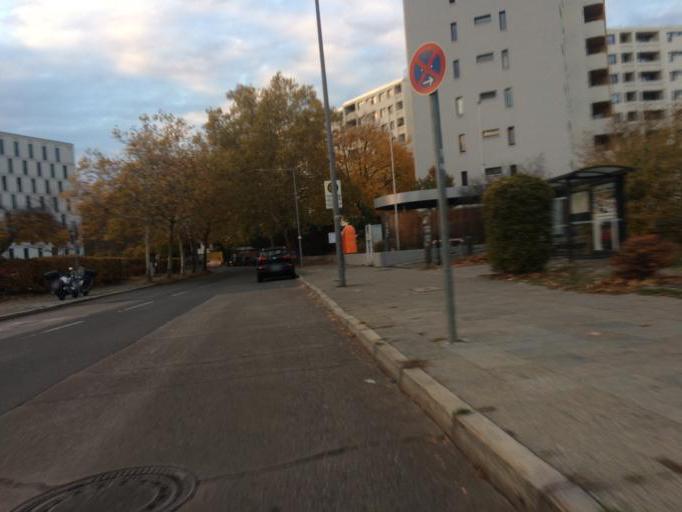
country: DE
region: Berlin
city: Markisches Viertel
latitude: 52.6045
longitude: 13.3620
